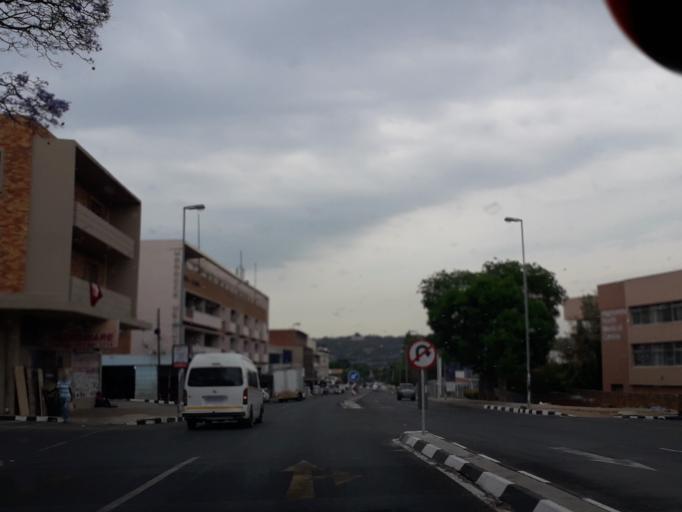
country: ZA
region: Gauteng
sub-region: City of Johannesburg Metropolitan Municipality
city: Johannesburg
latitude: -26.1460
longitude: 28.0868
